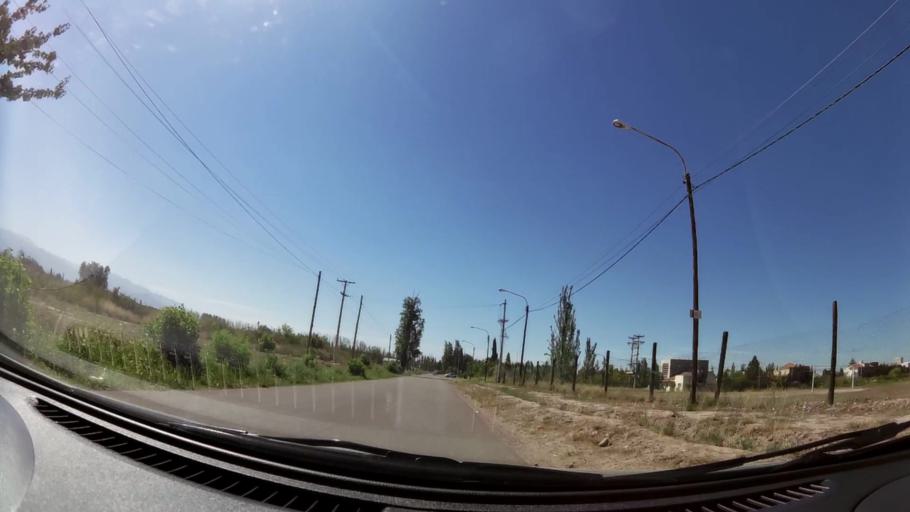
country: AR
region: Mendoza
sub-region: Departamento de Godoy Cruz
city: Godoy Cruz
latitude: -32.9831
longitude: -68.8432
